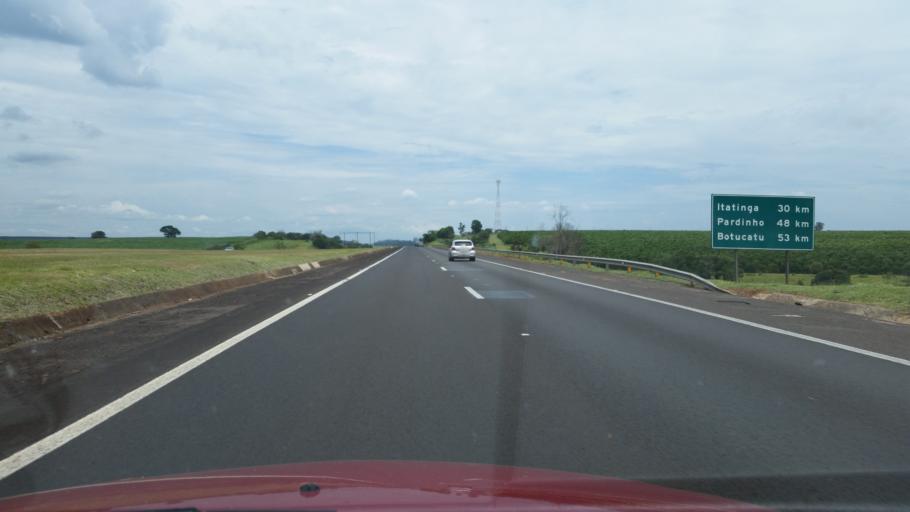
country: BR
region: Sao Paulo
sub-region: Avare
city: Avare
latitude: -22.9764
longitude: -48.7851
